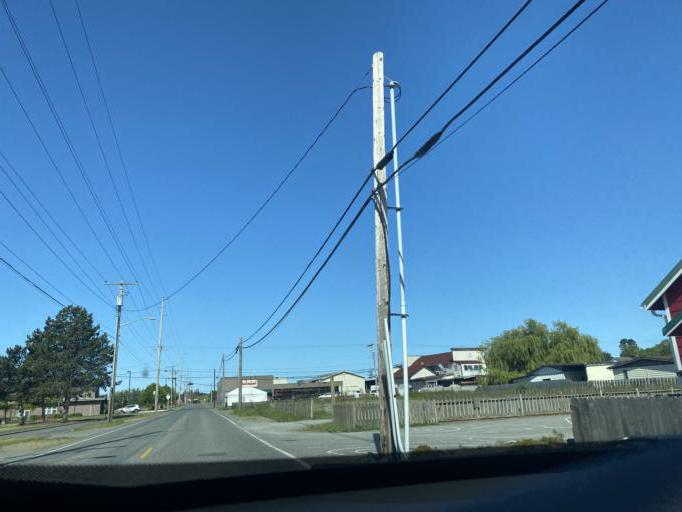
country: US
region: Washington
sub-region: Island County
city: Coupeville
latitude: 48.2074
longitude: -122.6845
